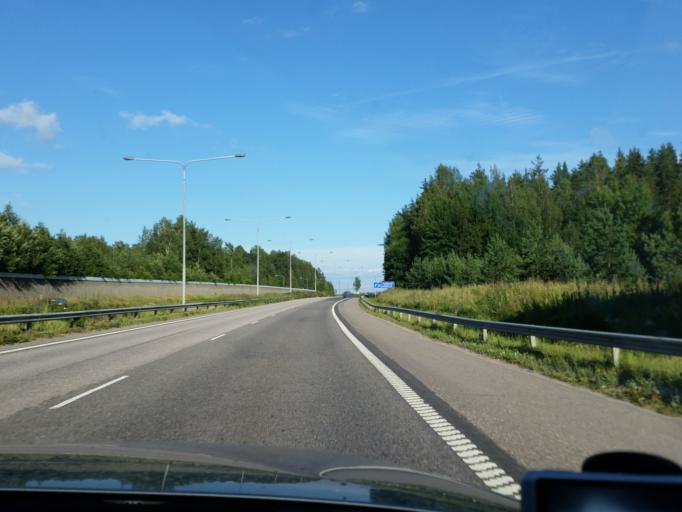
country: FI
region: Uusimaa
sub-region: Helsinki
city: Espoo
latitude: 60.2234
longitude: 24.6227
